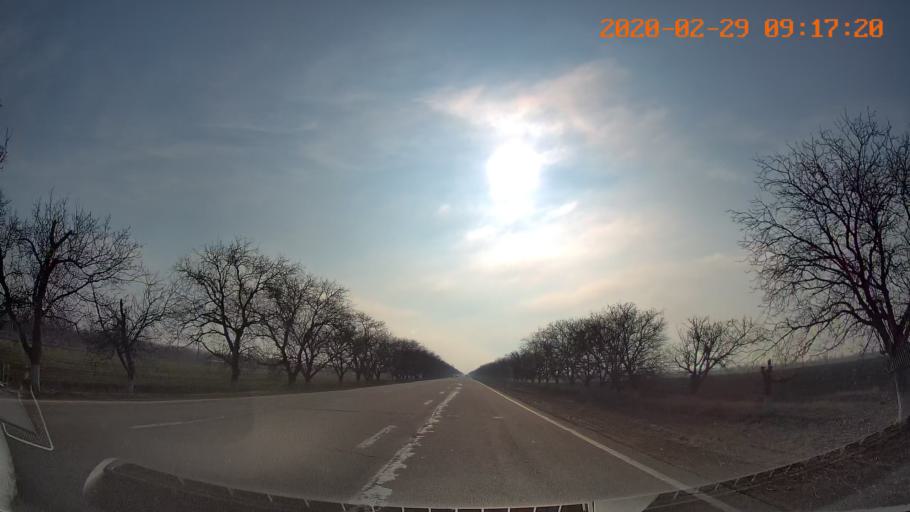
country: MD
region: Telenesti
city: Pervomaisc
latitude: 46.7840
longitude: 29.9022
